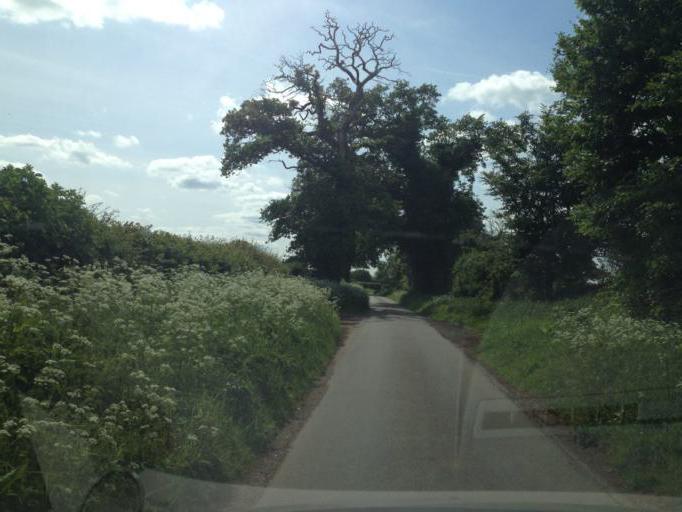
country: GB
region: England
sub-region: Buckinghamshire
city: Long Crendon
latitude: 51.7456
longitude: -1.0648
